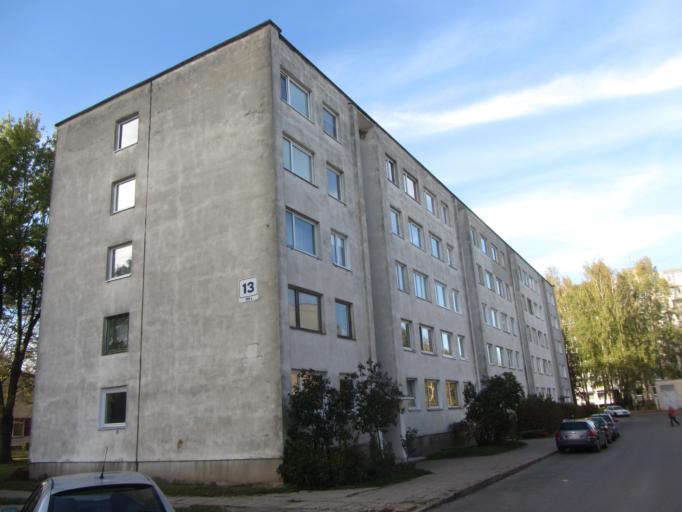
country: LT
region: Vilnius County
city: Elektrenai
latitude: 54.7875
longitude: 24.6629
